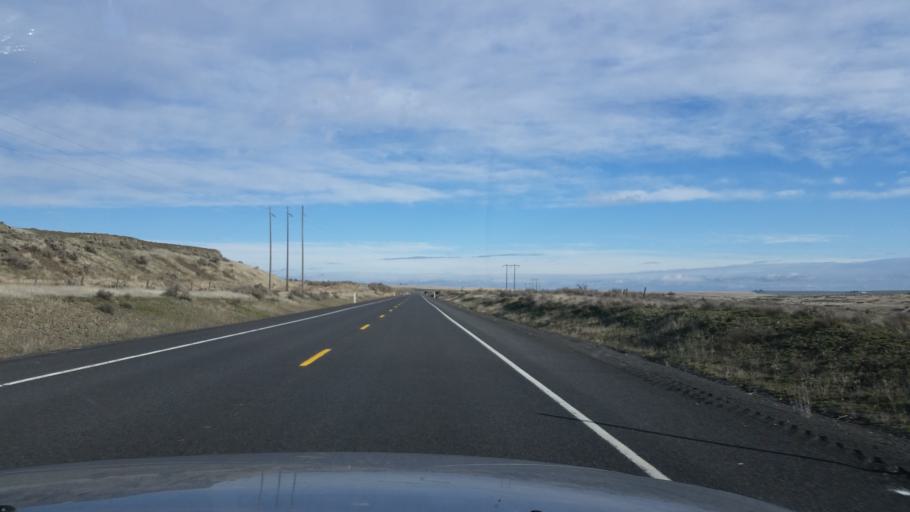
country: US
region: Washington
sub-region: Adams County
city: Ritzville
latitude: 47.3647
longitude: -118.4668
